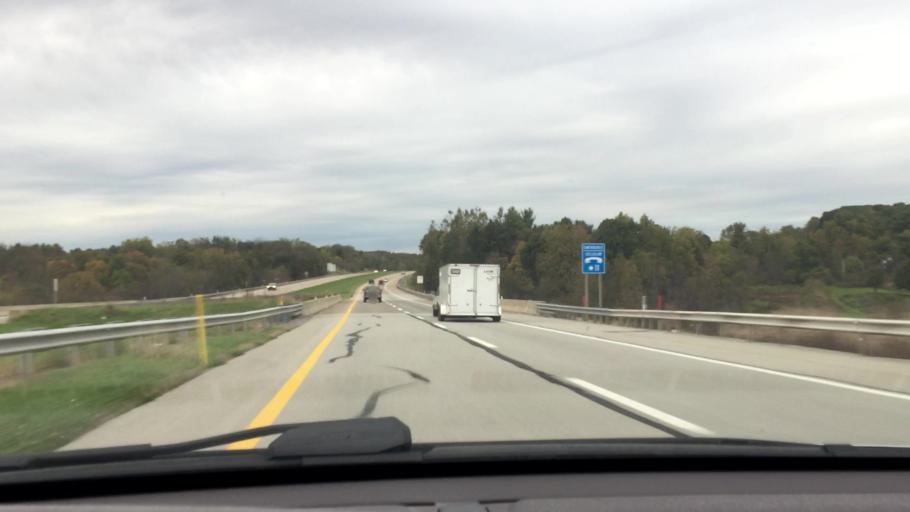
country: US
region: Pennsylvania
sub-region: Lawrence County
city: New Beaver
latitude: 40.8503
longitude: -80.3682
